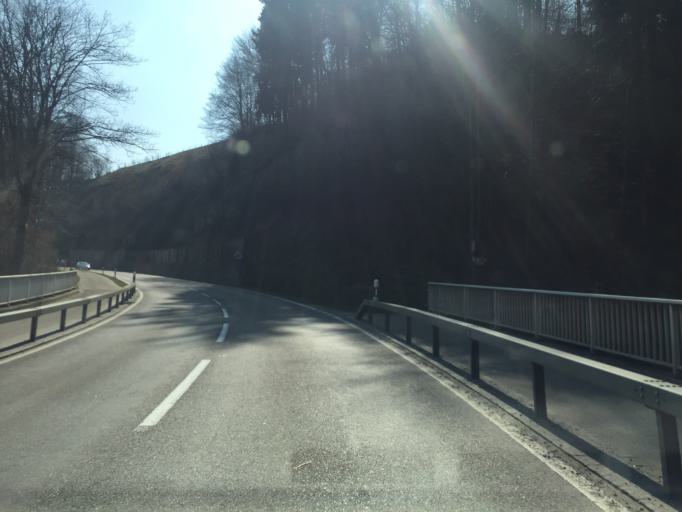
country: CH
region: Saint Gallen
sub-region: Wahlkreis Toggenburg
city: Lutisburg
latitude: 47.3929
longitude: 9.0729
